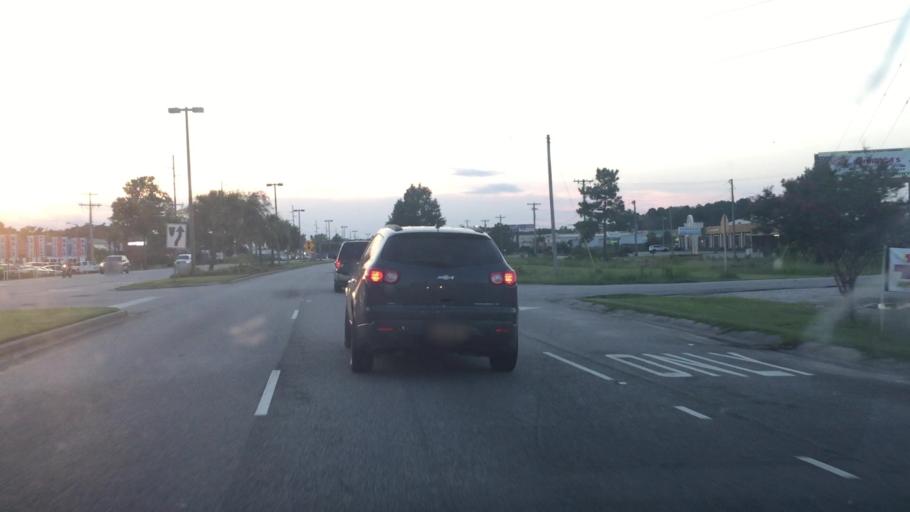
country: US
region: South Carolina
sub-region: Horry County
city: Myrtle Beach
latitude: 33.6996
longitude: -78.9004
